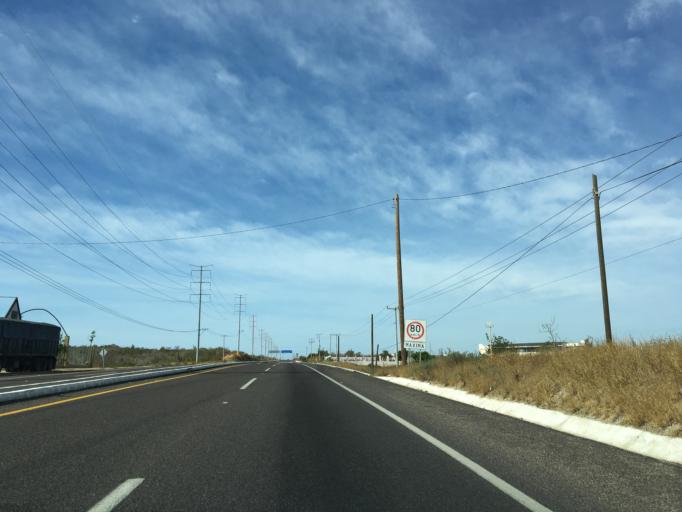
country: MX
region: Baja California Sur
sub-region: Los Cabos
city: Las Palmas
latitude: 22.9223
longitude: -109.9757
